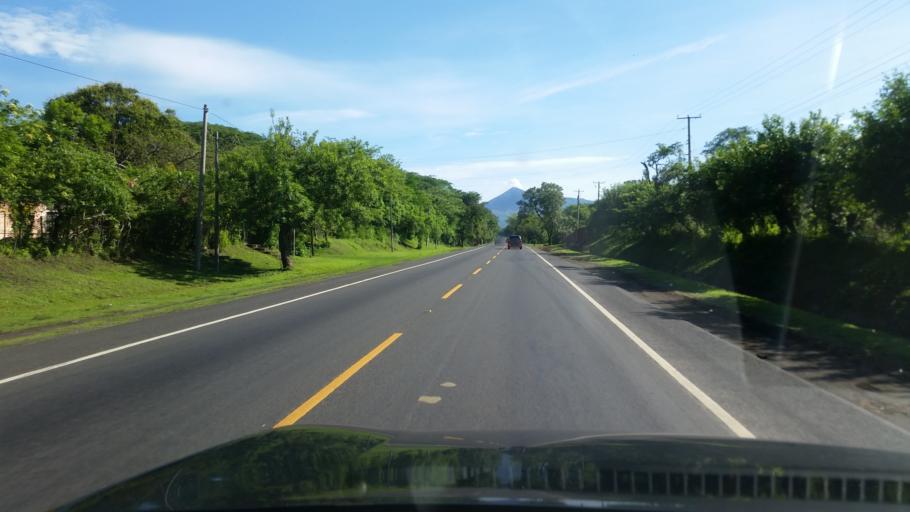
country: NI
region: Leon
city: Telica
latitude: 12.4850
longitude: -86.8615
